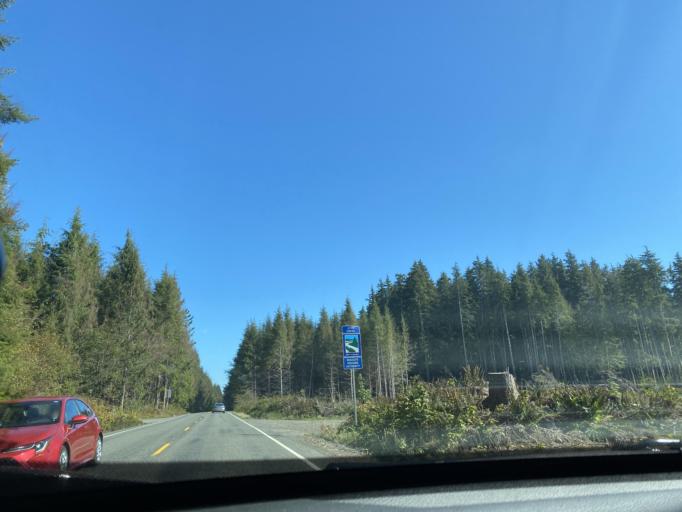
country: US
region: Washington
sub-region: Clallam County
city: Forks
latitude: 47.9188
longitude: -124.5189
